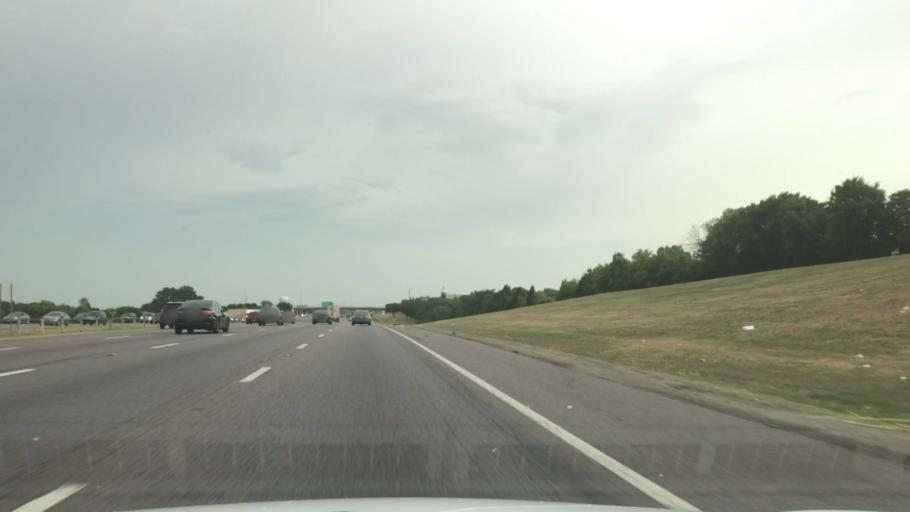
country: US
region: Texas
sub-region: Dallas County
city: Mesquite
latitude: 32.7616
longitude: -96.6201
